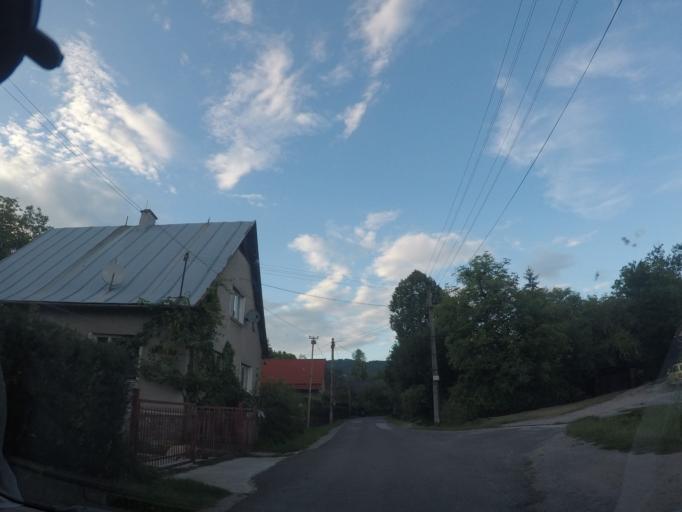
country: SK
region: Nitriansky
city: Prievidza
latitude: 48.8833
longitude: 18.6639
